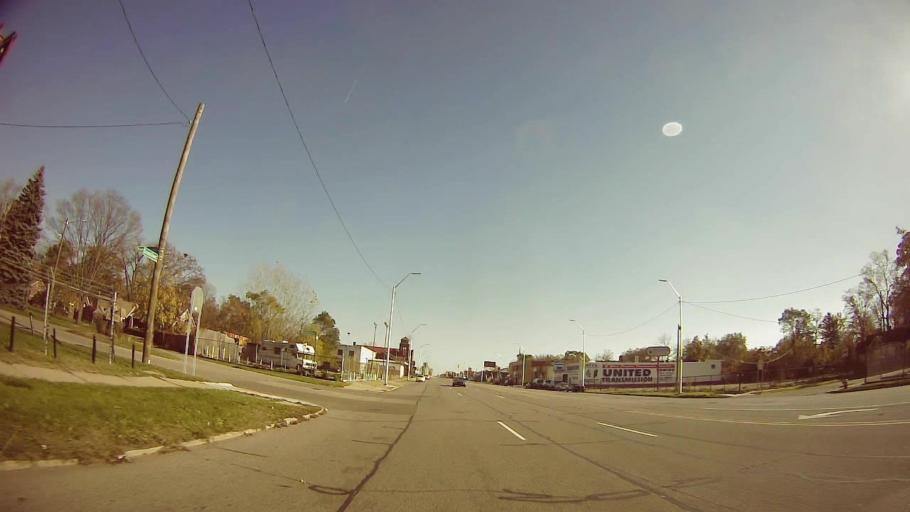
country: US
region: Michigan
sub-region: Wayne County
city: Redford
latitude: 42.4198
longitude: -83.2655
